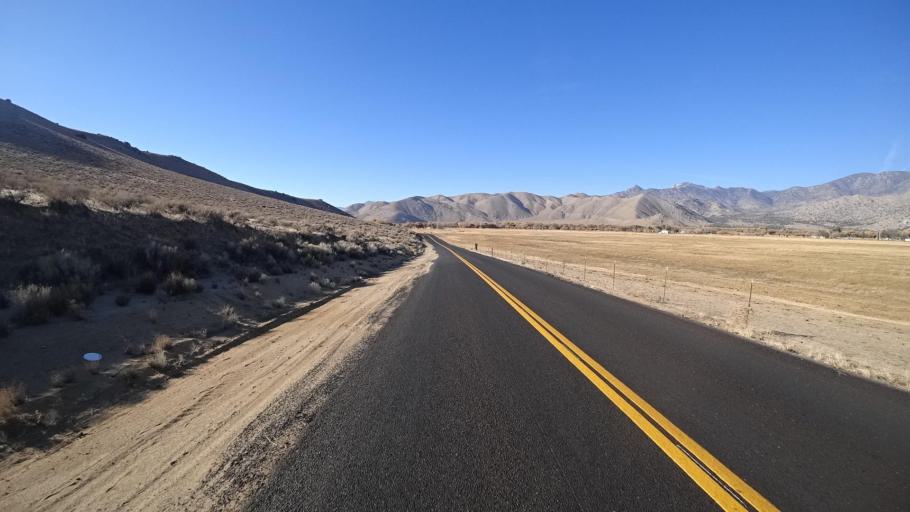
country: US
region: California
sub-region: Kern County
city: Weldon
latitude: 35.6597
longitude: -118.2925
